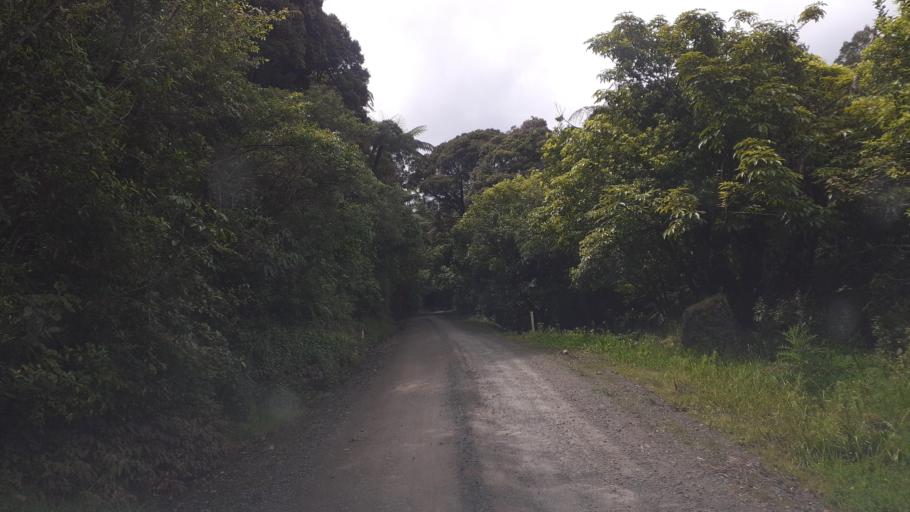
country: NZ
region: Northland
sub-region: Far North District
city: Waimate North
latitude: -35.5728
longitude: 173.5632
